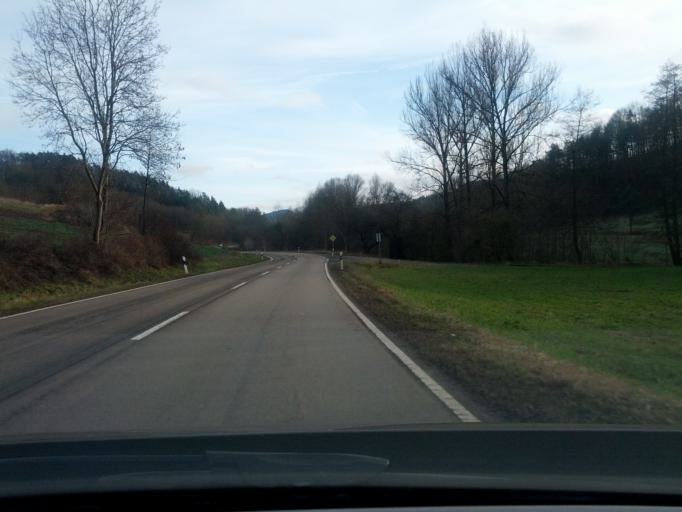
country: DE
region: Hesse
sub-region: Regierungsbezirk Kassel
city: Weissenborn
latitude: 51.1127
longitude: 10.0460
